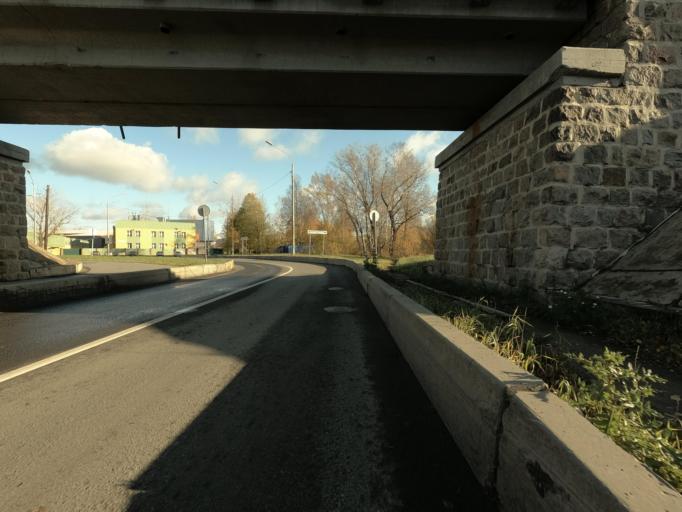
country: RU
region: St.-Petersburg
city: Krasnogvargeisky
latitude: 59.9482
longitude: 30.4471
